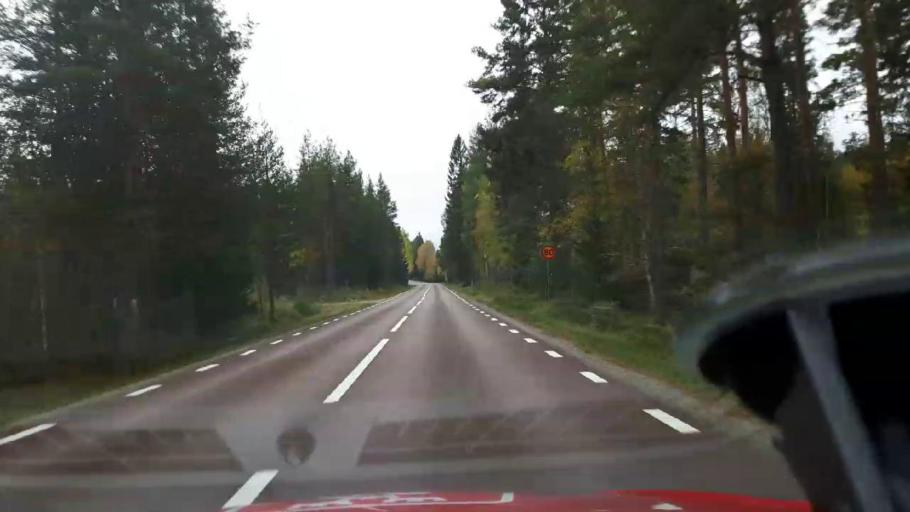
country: SE
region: Jaemtland
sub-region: Harjedalens Kommun
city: Sveg
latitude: 62.2165
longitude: 14.8466
